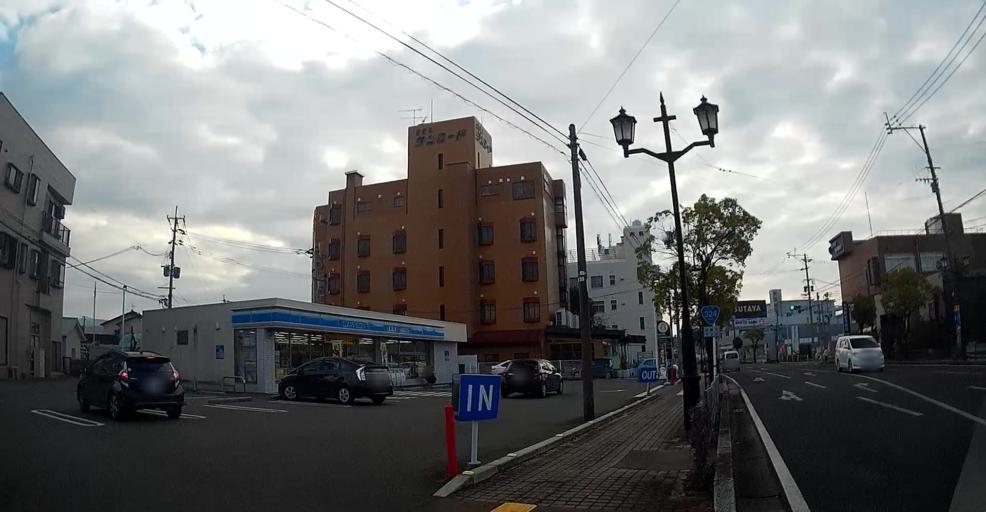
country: JP
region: Kumamoto
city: Hondo
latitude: 32.4549
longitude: 130.1942
